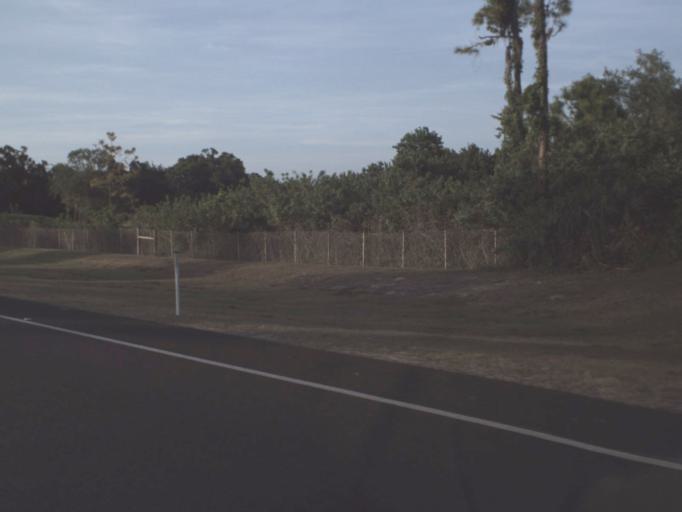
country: US
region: Florida
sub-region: Brevard County
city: Mims
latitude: 28.6909
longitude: -80.8797
